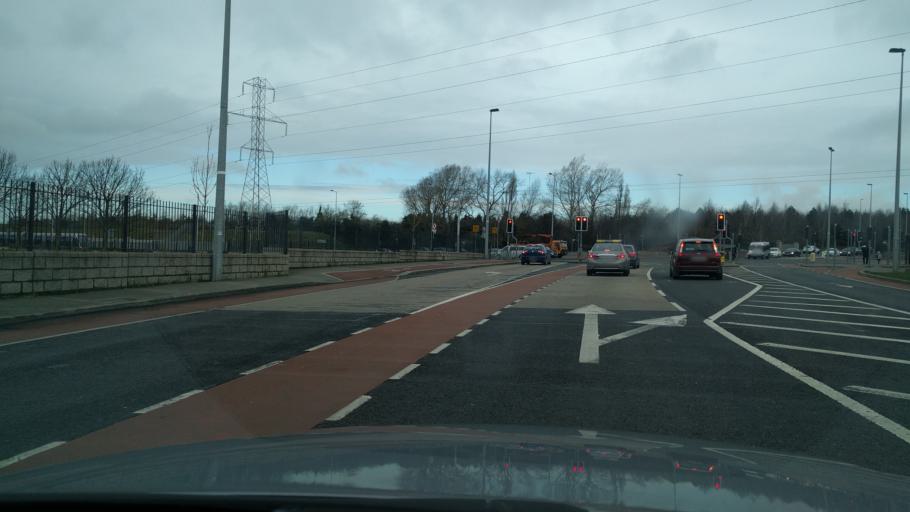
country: IE
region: Leinster
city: Tallaght
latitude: 53.2950
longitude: -6.3870
